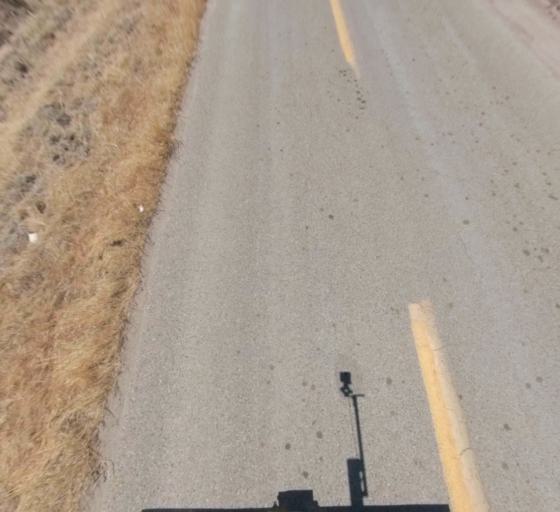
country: US
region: California
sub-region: Madera County
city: Parkwood
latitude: 36.8585
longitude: -120.1361
